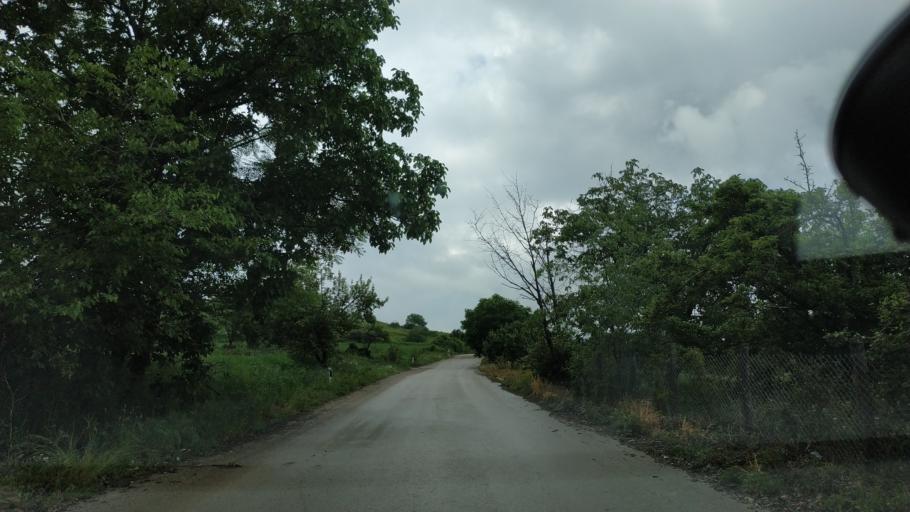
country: RS
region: Central Serbia
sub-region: Toplicki Okrug
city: Prokuplje
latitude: 43.4023
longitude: 21.5578
